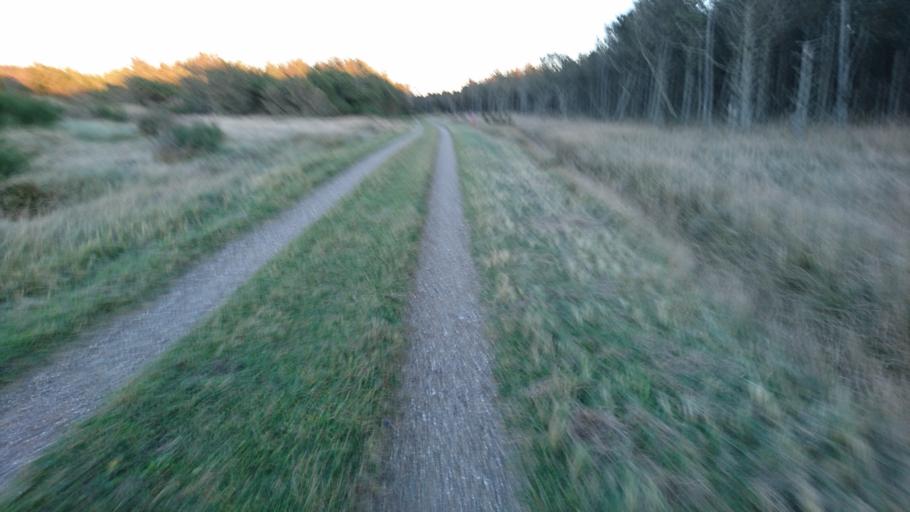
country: DK
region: North Denmark
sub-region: Frederikshavn Kommune
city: Skagen
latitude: 57.7127
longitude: 10.4996
